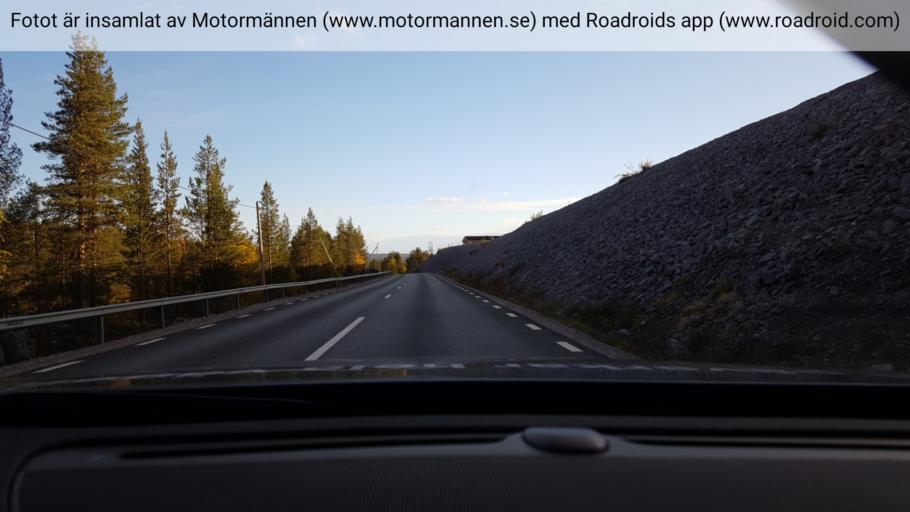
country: SE
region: Norrbotten
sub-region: Jokkmokks Kommun
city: Jokkmokk
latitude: 66.8881
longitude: 19.8283
